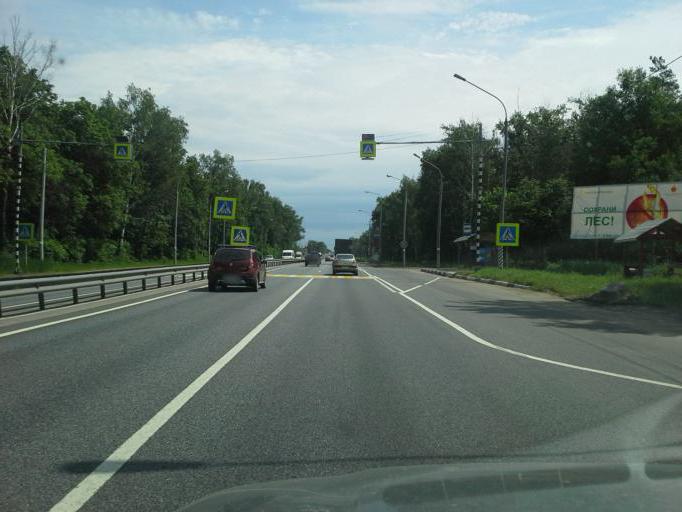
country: RU
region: Moskovskaya
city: Staraya Kupavna
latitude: 55.8160
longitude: 38.1354
